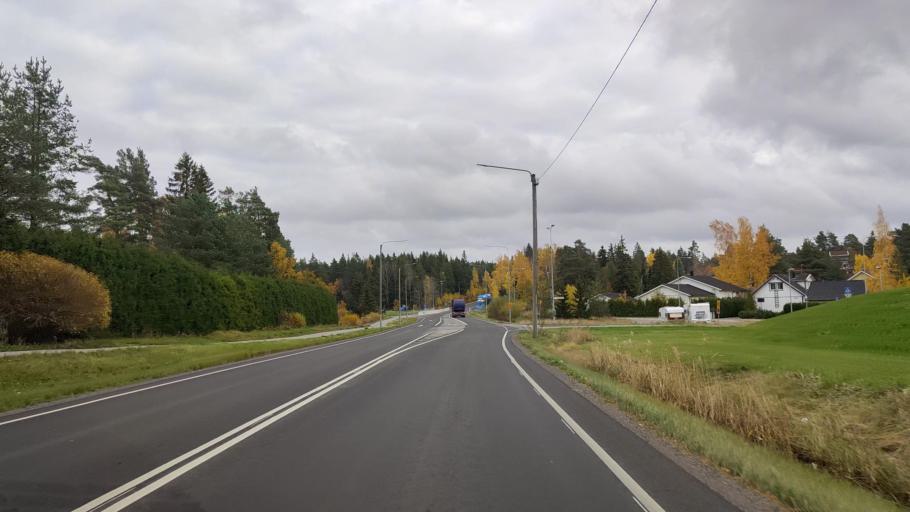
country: FI
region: Varsinais-Suomi
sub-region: Turku
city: Kaarina
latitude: 60.4617
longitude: 22.3572
